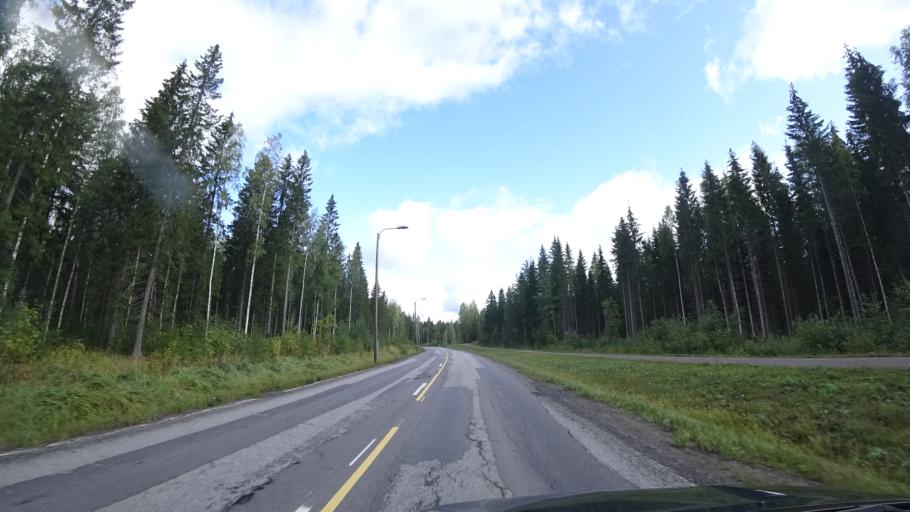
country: FI
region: Uusimaa
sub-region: Helsinki
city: Hyvinge
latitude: 60.5703
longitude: 24.9775
